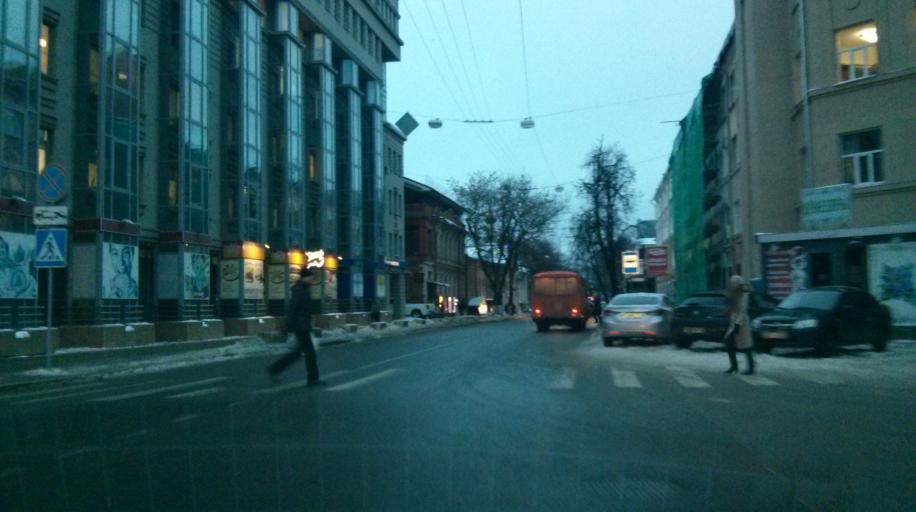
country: RU
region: Nizjnij Novgorod
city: Nizhniy Novgorod
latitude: 56.3284
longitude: 44.0156
